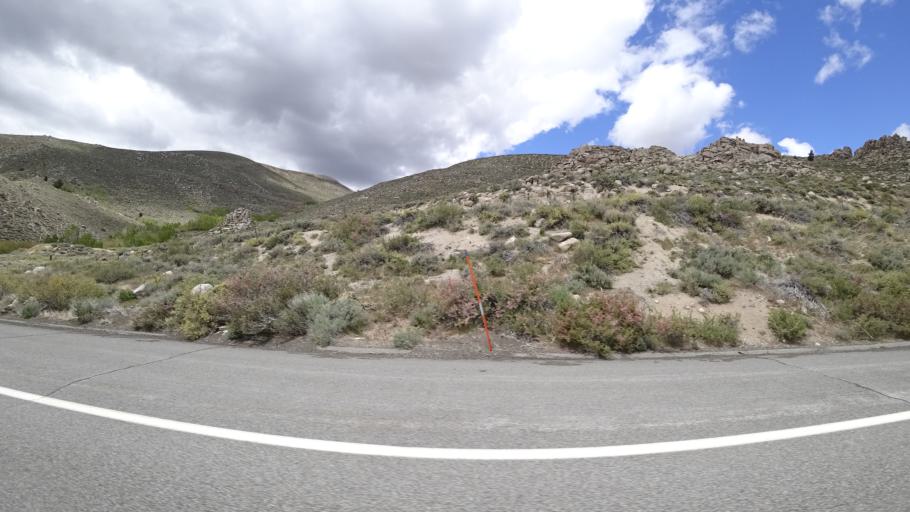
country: US
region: California
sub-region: Mono County
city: Bridgeport
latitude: 38.0712
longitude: -119.1691
